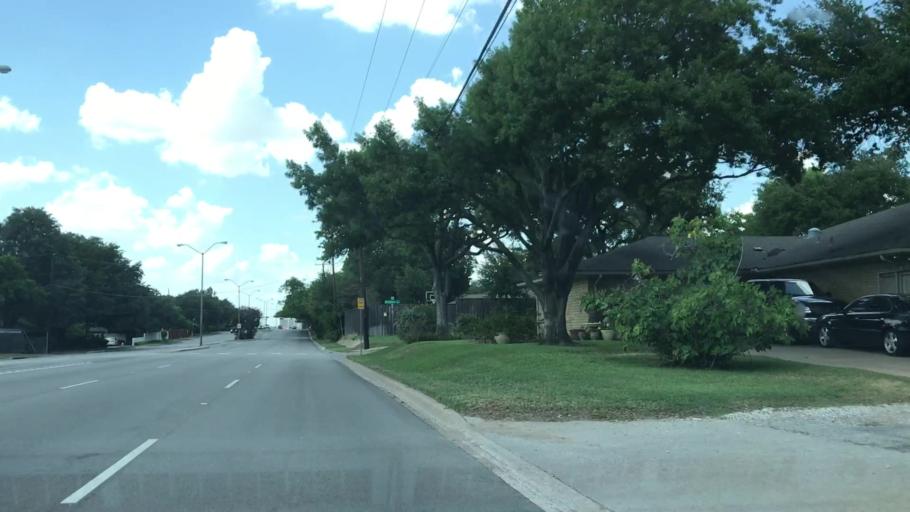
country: US
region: Texas
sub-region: Dallas County
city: Addison
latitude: 32.9177
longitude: -96.8381
